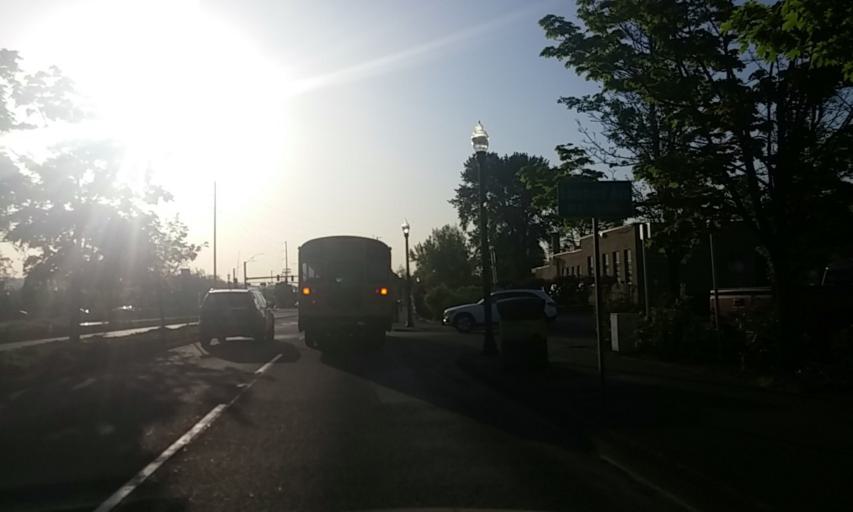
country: US
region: Oregon
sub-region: Washington County
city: Beaverton
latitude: 45.4867
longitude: -122.8023
